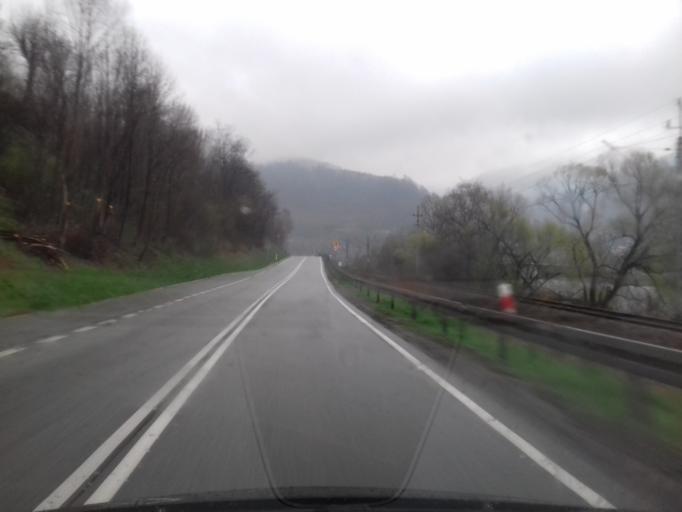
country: PL
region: Lesser Poland Voivodeship
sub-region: Powiat nowosadecki
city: Piwniczna-Zdroj
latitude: 49.4624
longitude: 20.6959
